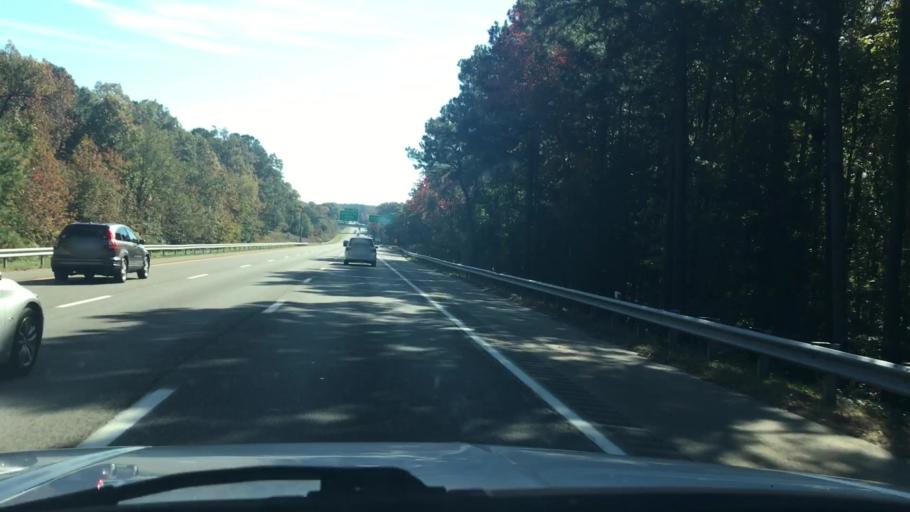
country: US
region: Virginia
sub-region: Henrico County
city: Short Pump
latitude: 37.6389
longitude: -77.5818
